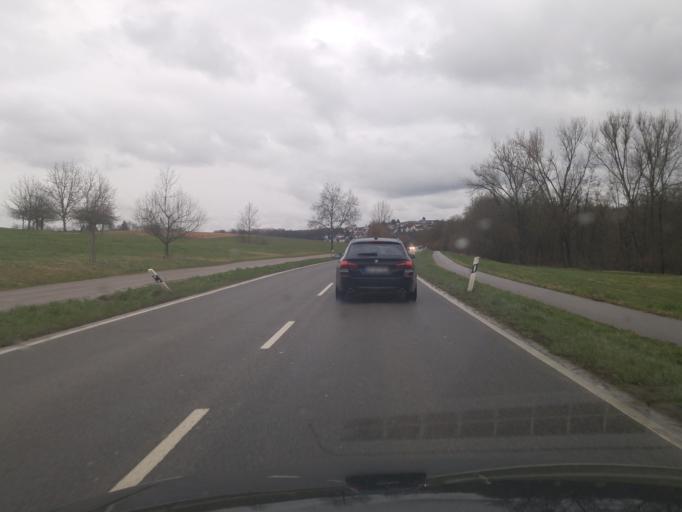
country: DE
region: Baden-Wuerttemberg
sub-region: Regierungsbezirk Stuttgart
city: Steinheim am der Murr
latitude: 48.9577
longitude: 9.2937
